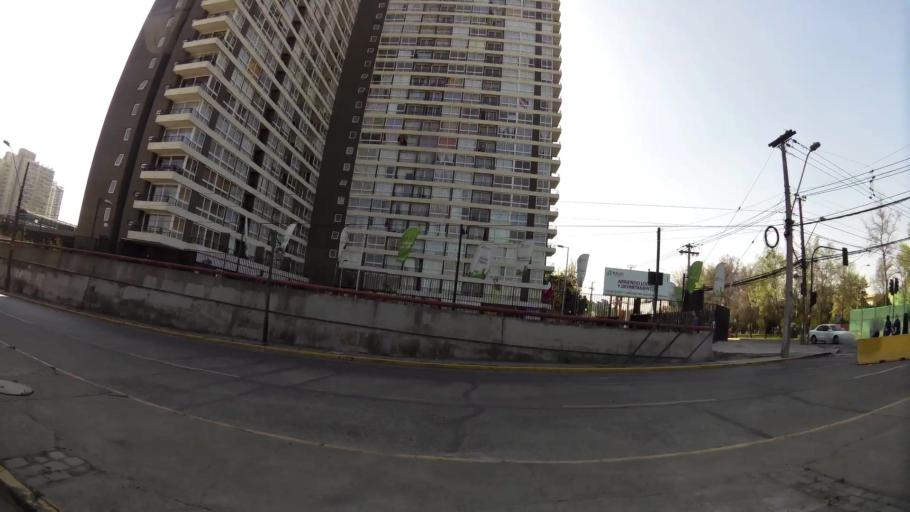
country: CL
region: Santiago Metropolitan
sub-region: Provincia de Santiago
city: Santiago
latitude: -33.4670
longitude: -70.6238
